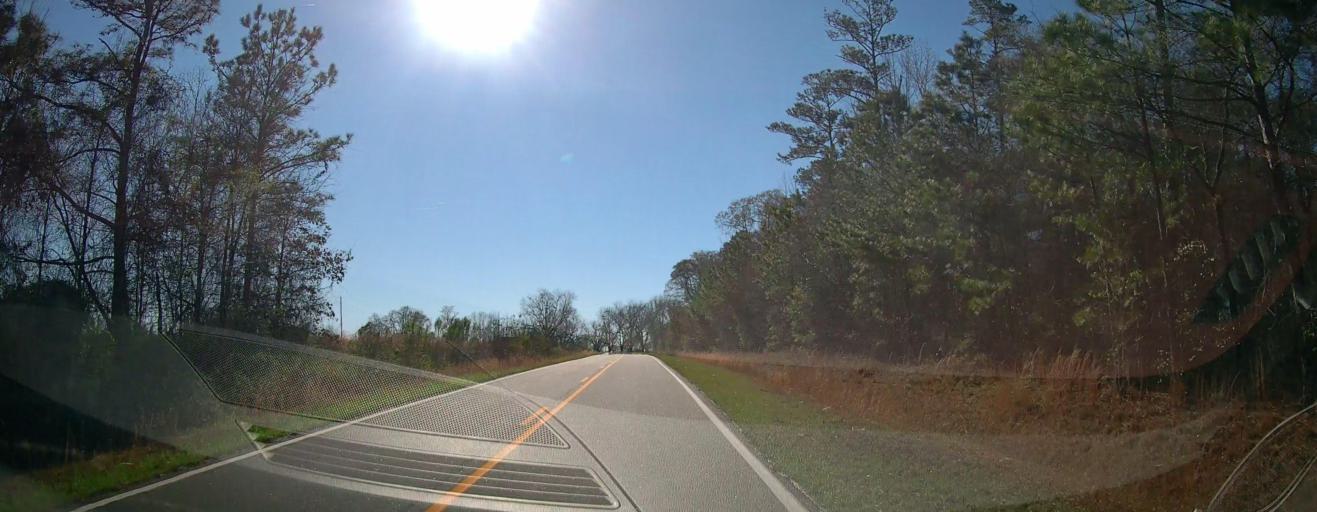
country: US
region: Georgia
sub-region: Peach County
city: Byron
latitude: 32.6752
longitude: -83.8166
